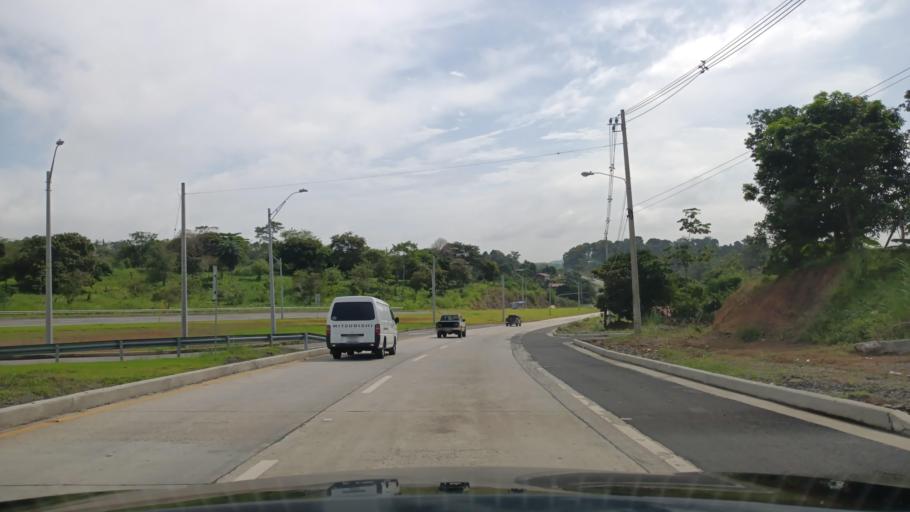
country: PA
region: Panama
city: Las Cumbres
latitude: 9.1011
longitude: -79.5177
